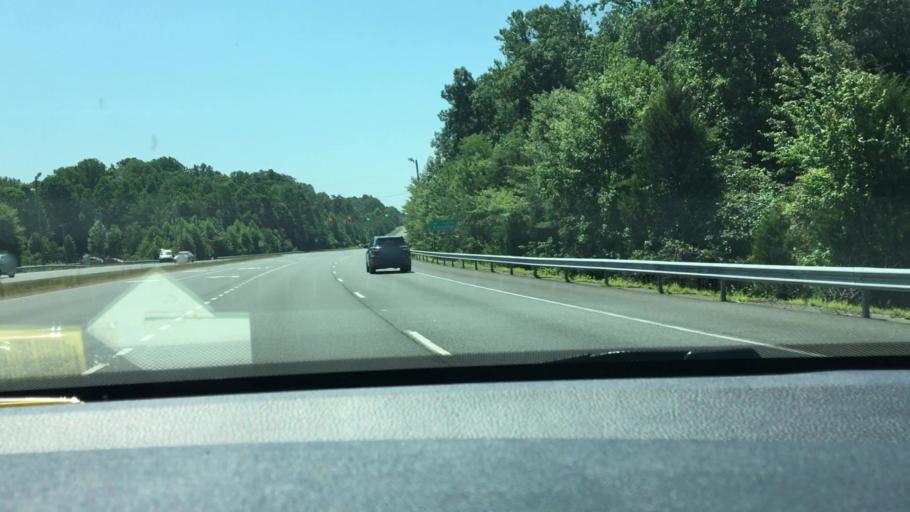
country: US
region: Virginia
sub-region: Prince William County
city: Buckhall
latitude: 38.7313
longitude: -77.4243
